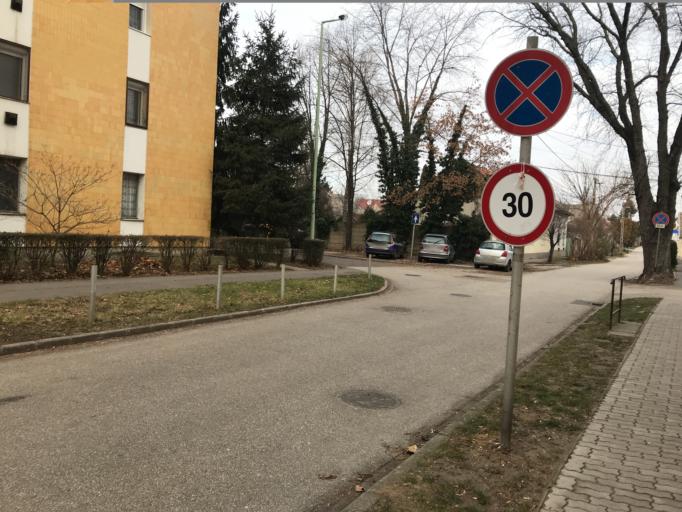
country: HU
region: Csongrad
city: Csongrad
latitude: 46.7107
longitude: 20.1470
